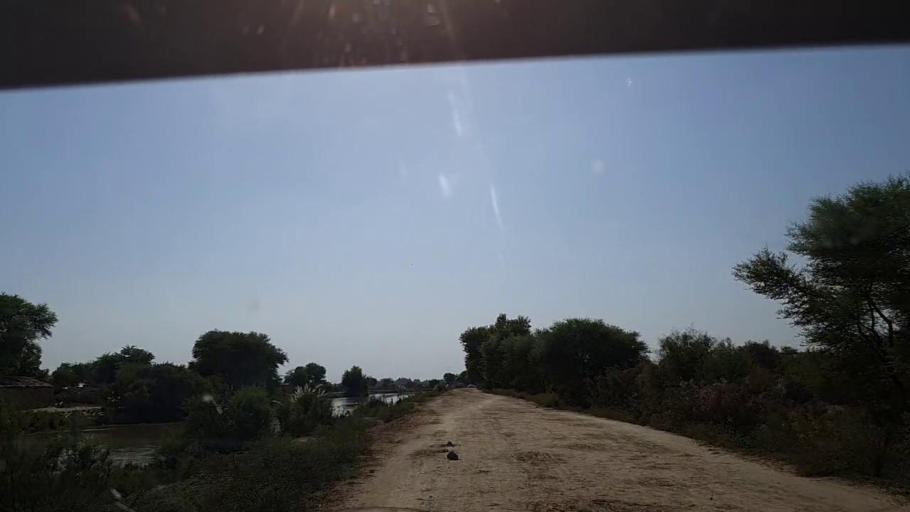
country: PK
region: Sindh
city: Ghauspur
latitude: 28.1842
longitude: 69.0774
